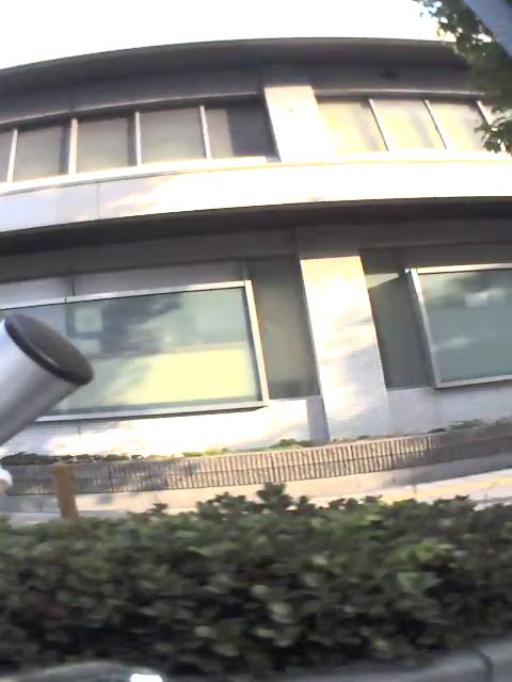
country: JP
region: Osaka
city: Moriguchi
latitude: 34.7327
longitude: 135.5567
